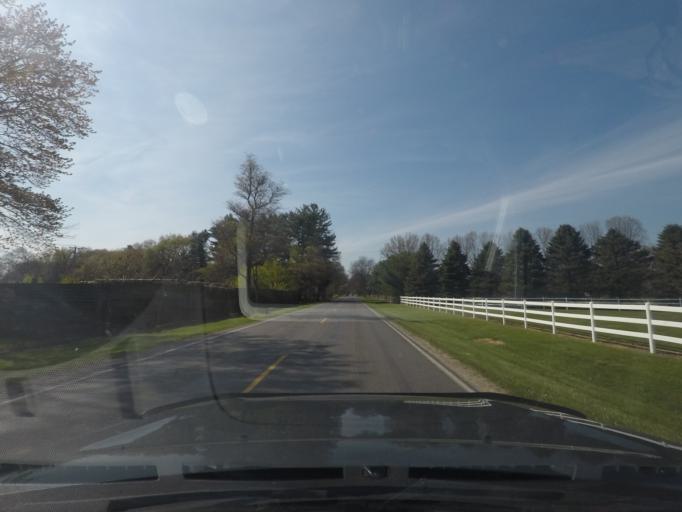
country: US
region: Indiana
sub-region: Elkhart County
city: Elkhart
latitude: 41.7151
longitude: -86.0302
